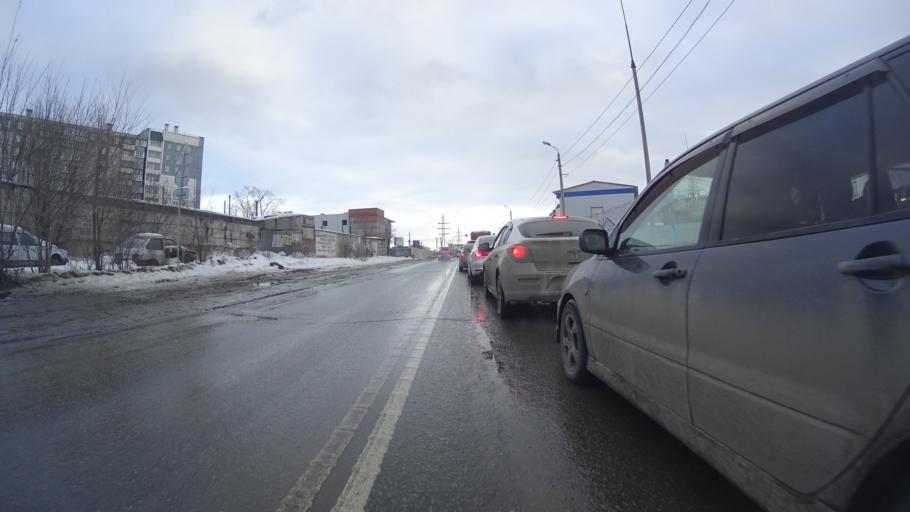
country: RU
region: Chelyabinsk
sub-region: Gorod Chelyabinsk
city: Chelyabinsk
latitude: 55.1396
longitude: 61.4017
